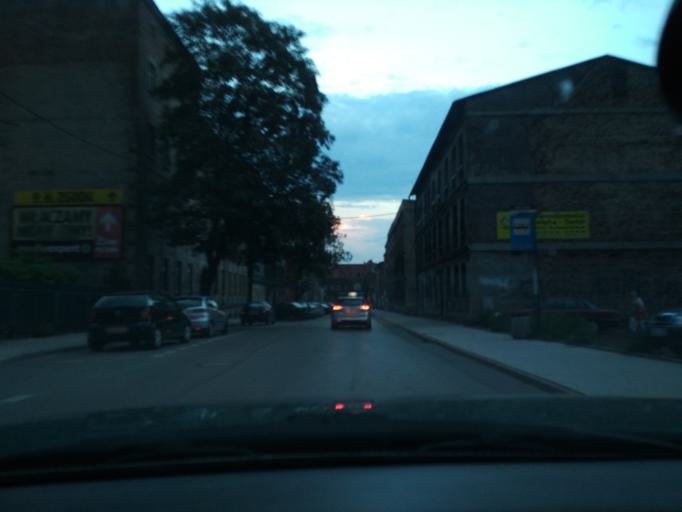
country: PL
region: Silesian Voivodeship
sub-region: Swietochlowice
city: Swietochlowice
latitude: 50.2898
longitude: 18.9186
